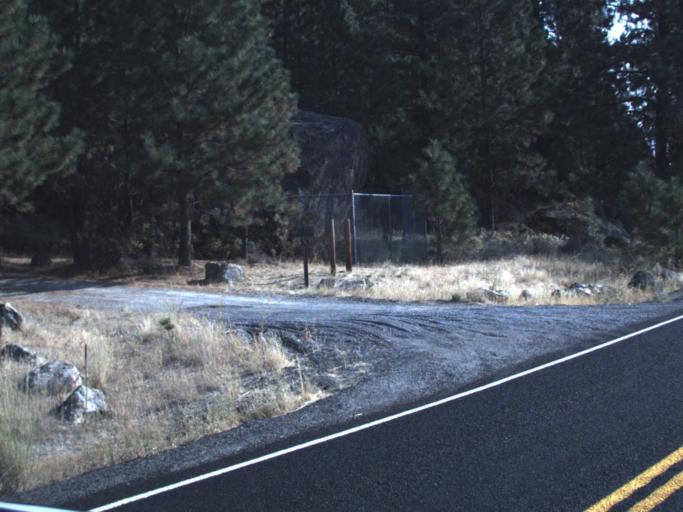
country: US
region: Washington
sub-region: Spokane County
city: Fairchild Air Force Base
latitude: 47.8380
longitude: -117.7558
